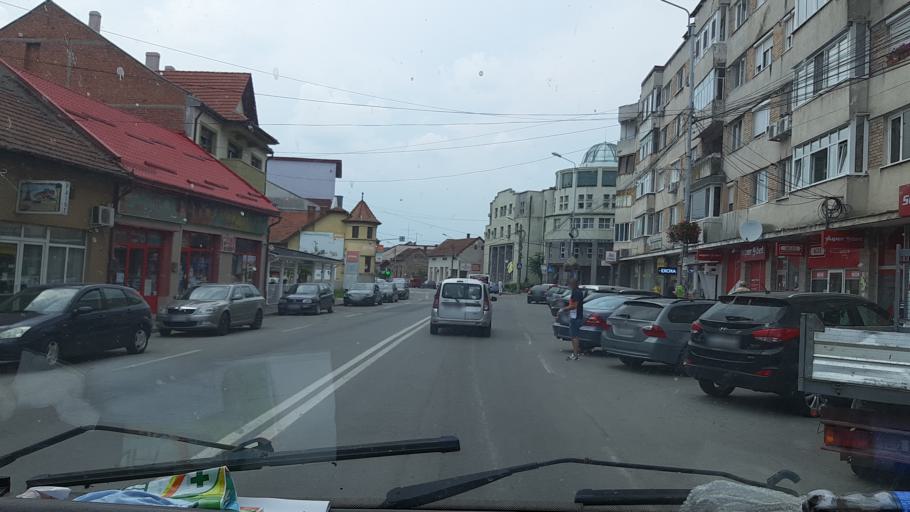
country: RO
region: Timis
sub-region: Municipiul Lugoj
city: Lugoj
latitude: 45.6904
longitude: 21.9031
